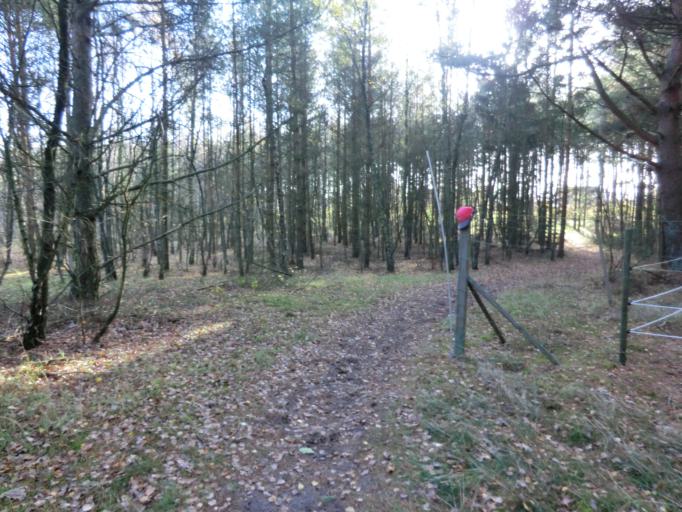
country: SE
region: Skane
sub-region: Hoors Kommun
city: Loberod
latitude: 55.7289
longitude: 13.3865
